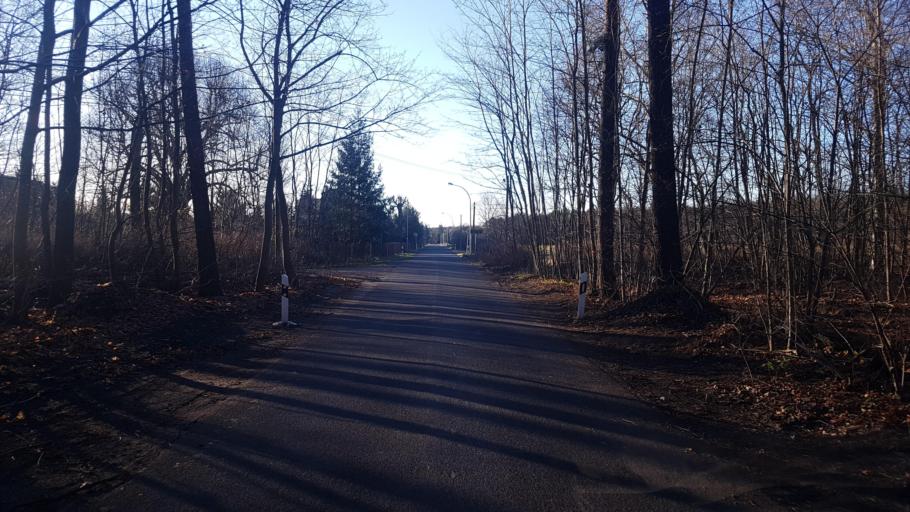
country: DE
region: Brandenburg
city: Tauer
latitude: 51.9363
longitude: 14.4725
